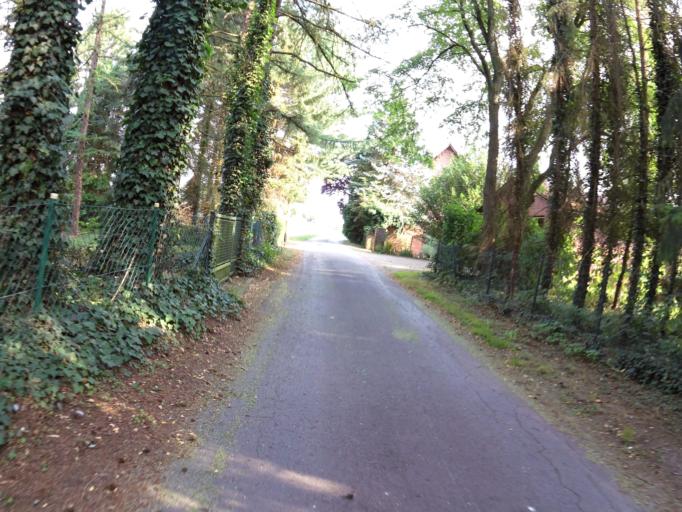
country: DE
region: Lower Saxony
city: Raddestorf
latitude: 52.4524
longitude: 9.0112
